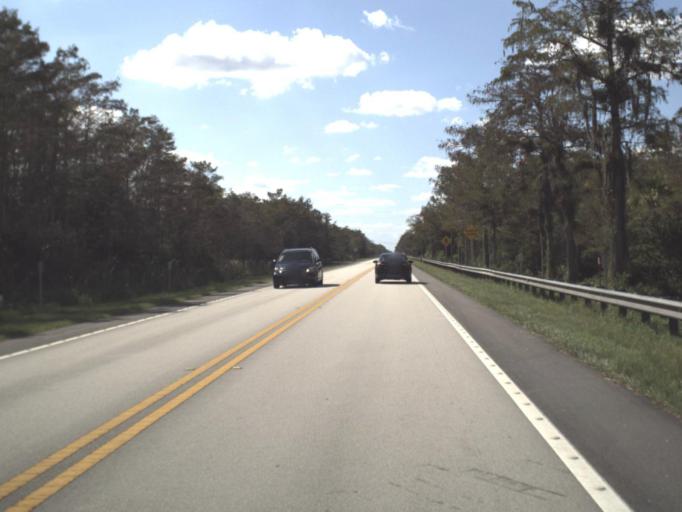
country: US
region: Florida
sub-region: Miami-Dade County
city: Kendall West
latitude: 25.8462
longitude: -80.9272
